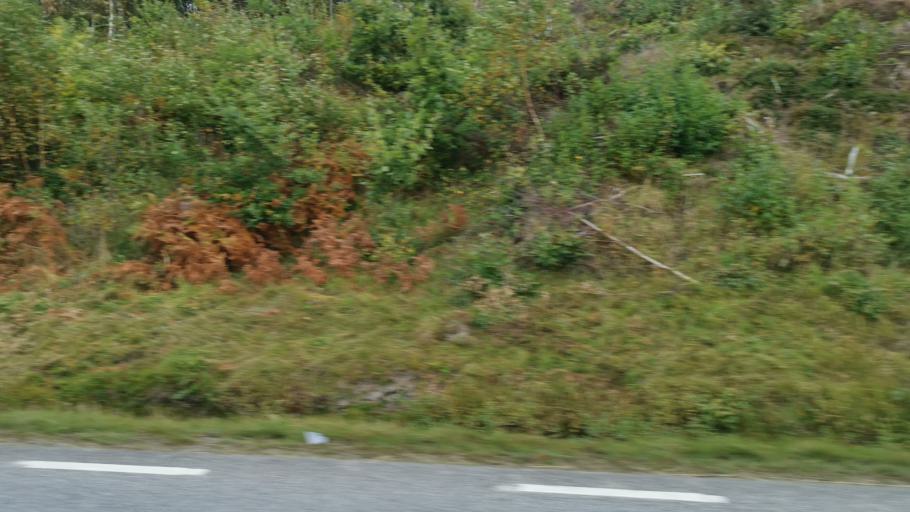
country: SE
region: Vaestra Goetaland
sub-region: Sotenas Kommun
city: Hunnebostrand
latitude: 58.5701
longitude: 11.3562
